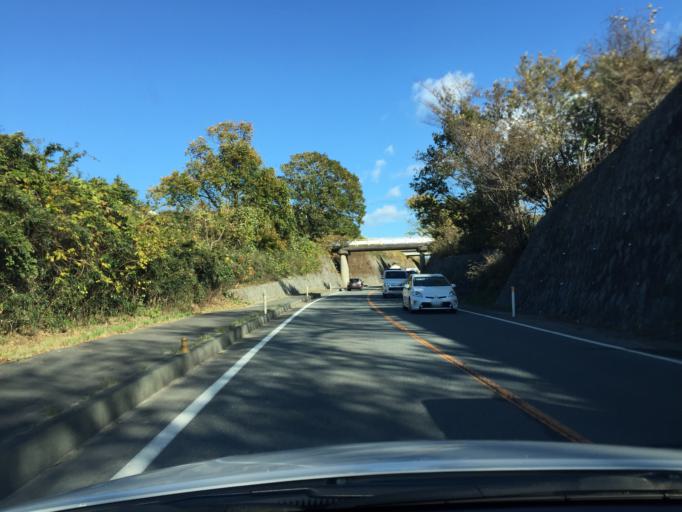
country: JP
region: Fukushima
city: Iwaki
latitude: 37.2097
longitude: 140.9934
